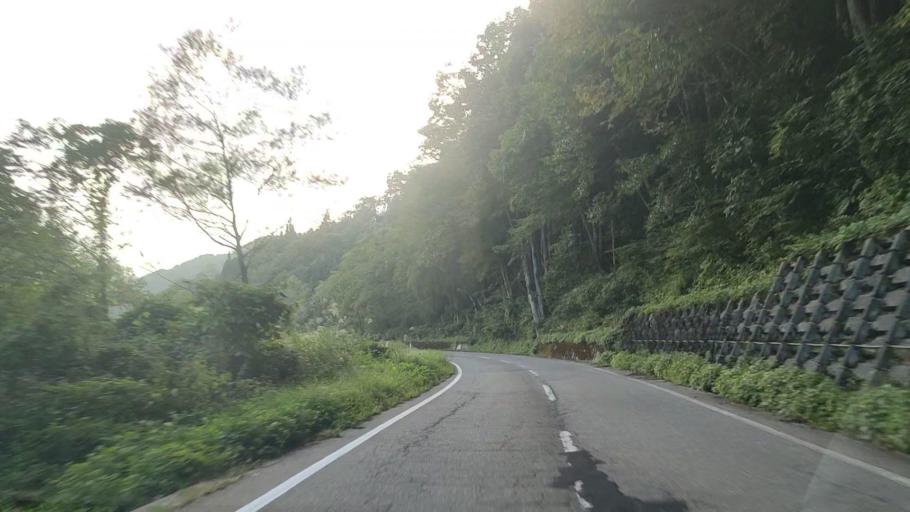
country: JP
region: Toyama
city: Yatsuomachi-higashikumisaka
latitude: 36.4626
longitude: 137.0445
